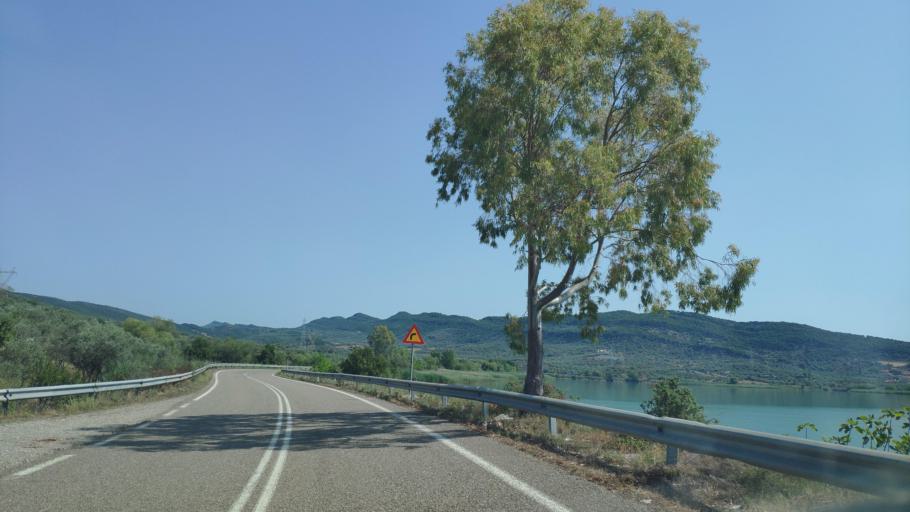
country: GR
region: West Greece
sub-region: Nomos Aitolias kai Akarnanias
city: Lepenou
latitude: 38.6995
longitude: 21.3215
